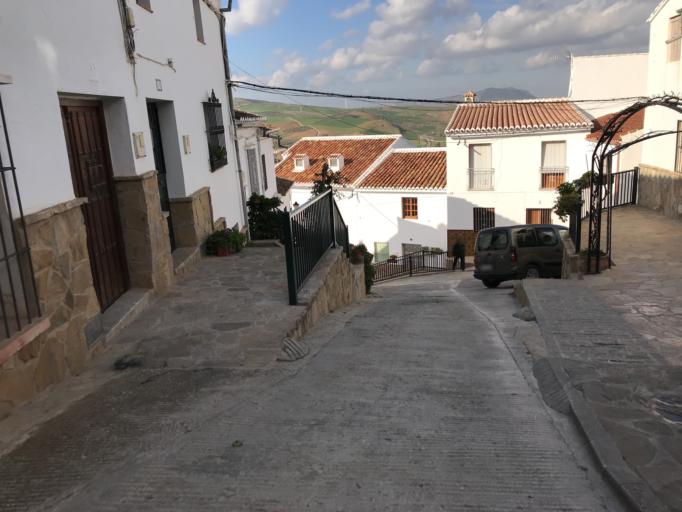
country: ES
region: Andalusia
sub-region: Provincia de Malaga
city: Ardales
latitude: 36.8770
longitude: -4.8458
